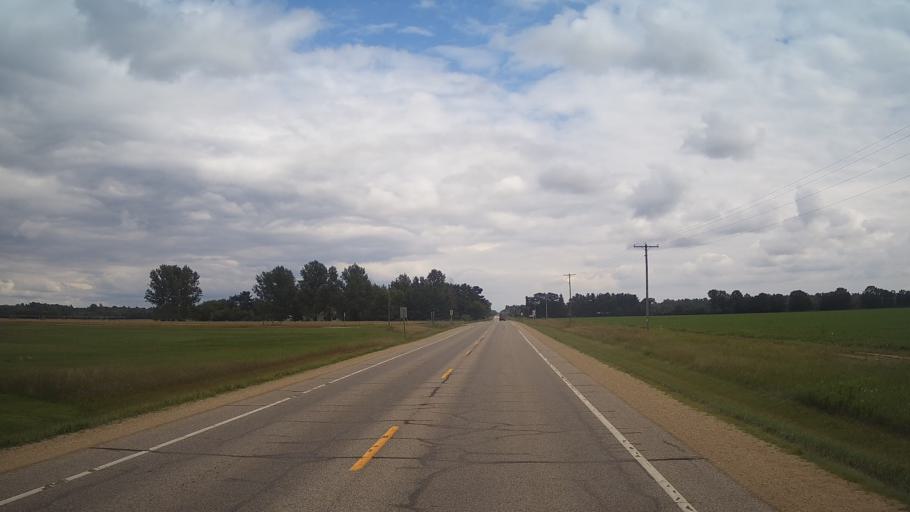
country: US
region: Wisconsin
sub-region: Waushara County
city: Wautoma
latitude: 44.0684
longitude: -89.3550
